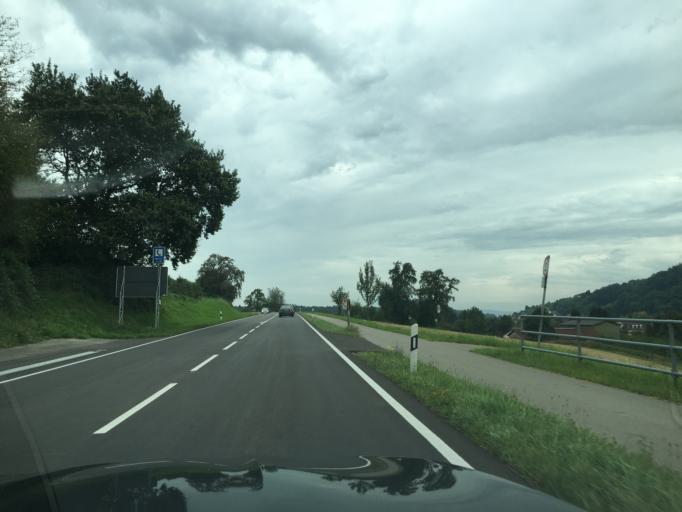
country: DE
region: Baden-Wuerttemberg
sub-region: Freiburg Region
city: Steisslingen
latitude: 47.7918
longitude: 8.9800
